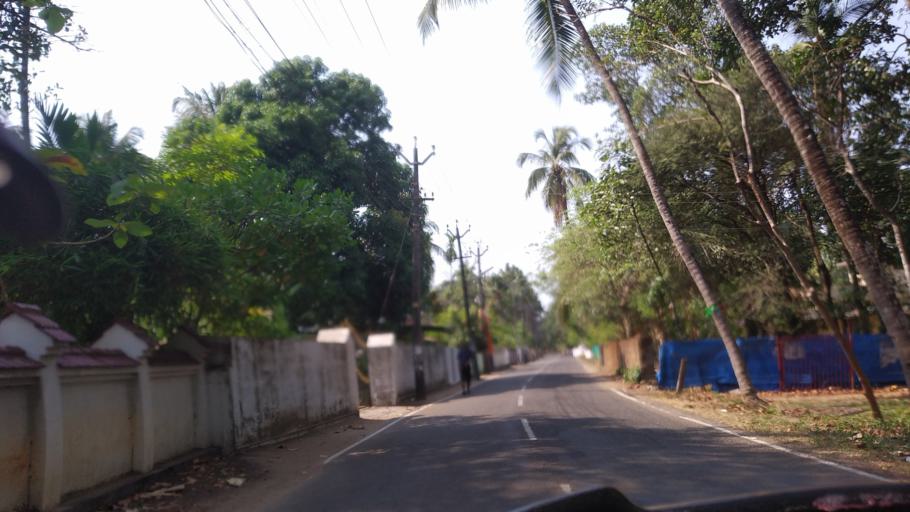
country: IN
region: Kerala
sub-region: Thrissur District
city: Thanniyam
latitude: 10.4118
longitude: 76.0934
